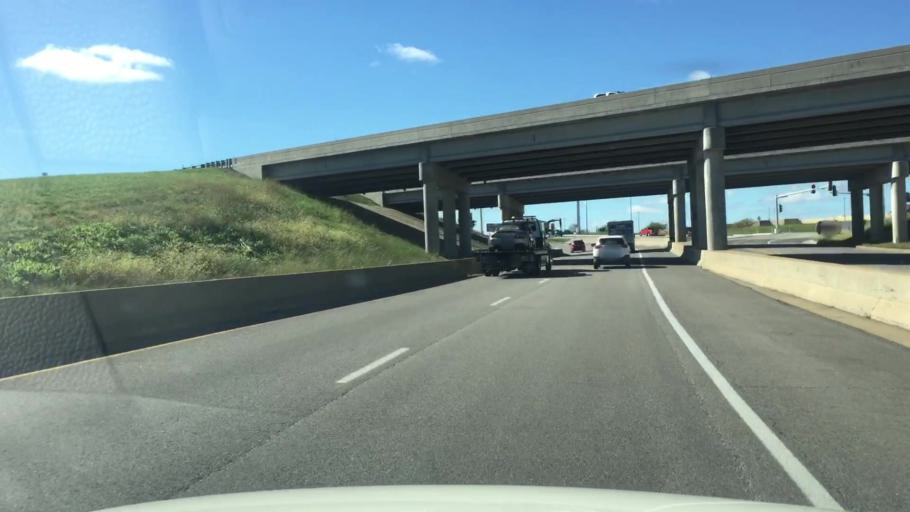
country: US
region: Missouri
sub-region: Boone County
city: Columbia
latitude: 38.9581
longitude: -92.2933
